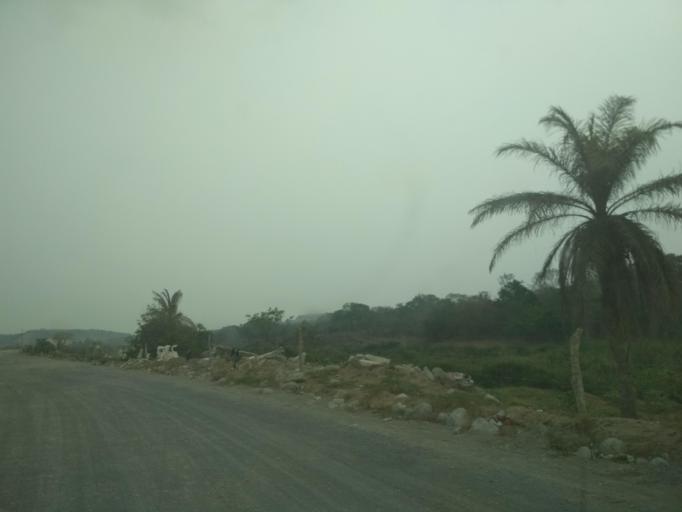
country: MX
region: Veracruz
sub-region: Veracruz
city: Fraccionamiento Geovillas los Pinos
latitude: 19.2250
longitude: -96.2271
